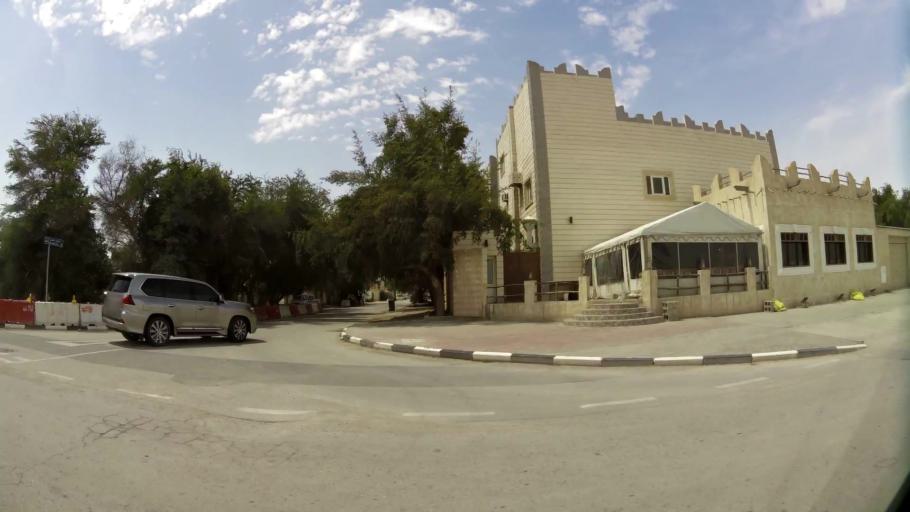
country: QA
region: Baladiyat ar Rayyan
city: Ar Rayyan
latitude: 25.2743
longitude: 51.4261
